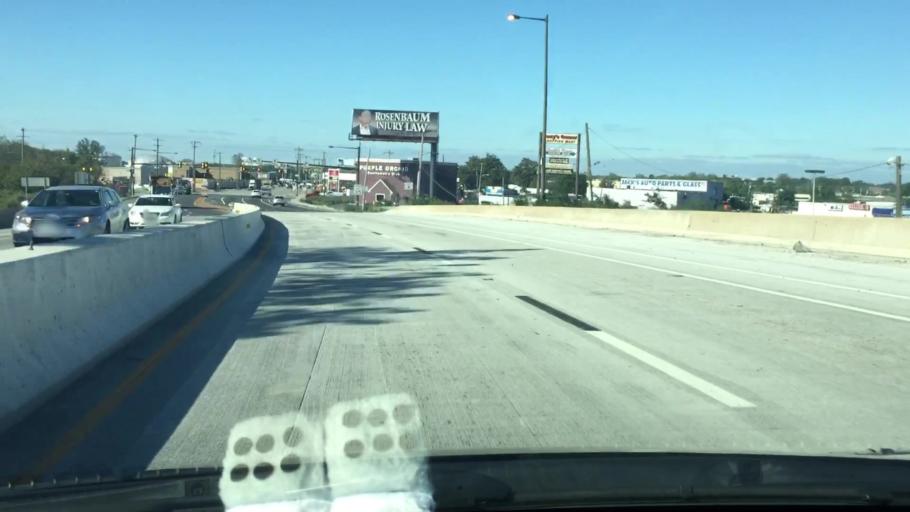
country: US
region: Pennsylvania
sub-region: Delaware County
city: Colwyn
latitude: 39.9189
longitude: -75.2067
